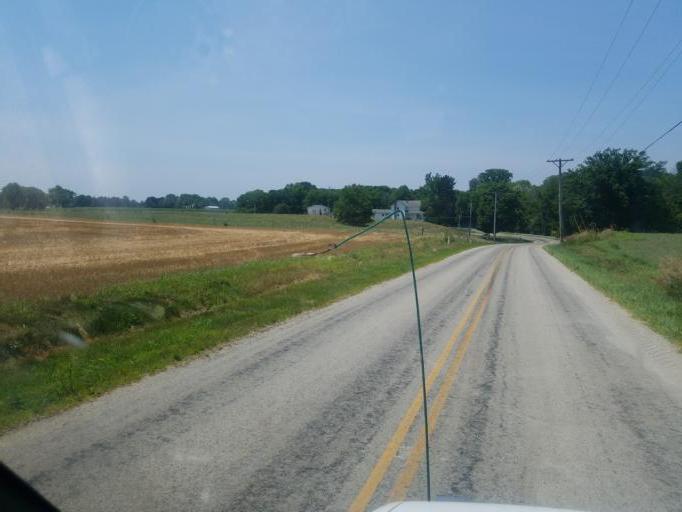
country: US
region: Ohio
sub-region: Shelby County
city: Sidney
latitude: 40.3063
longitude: -84.1131
